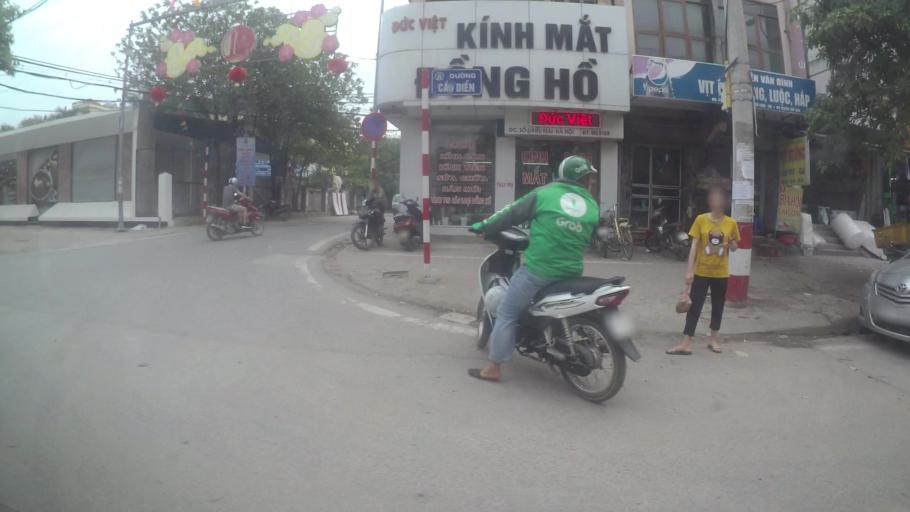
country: VN
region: Ha Noi
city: Cau Dien
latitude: 21.0447
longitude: 105.7528
